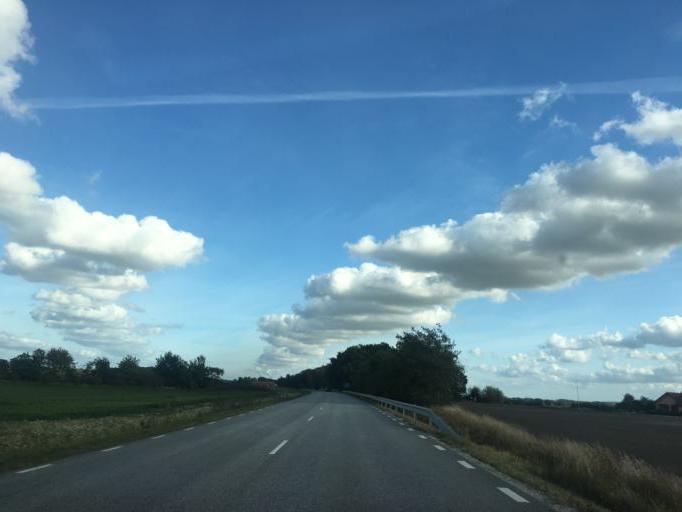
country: SE
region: Skane
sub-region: Lunds Kommun
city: Lund
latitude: 55.7929
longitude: 13.2137
